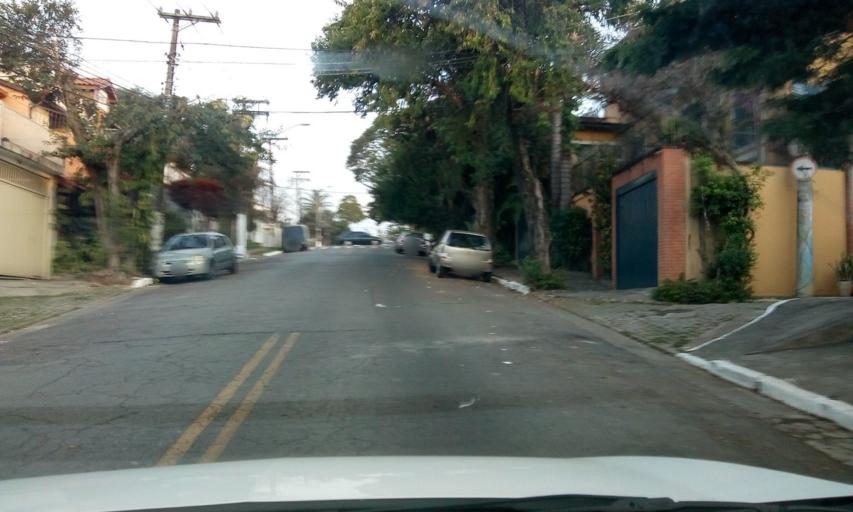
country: BR
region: Sao Paulo
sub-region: Sao Paulo
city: Sao Paulo
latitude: -23.6148
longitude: -46.6461
